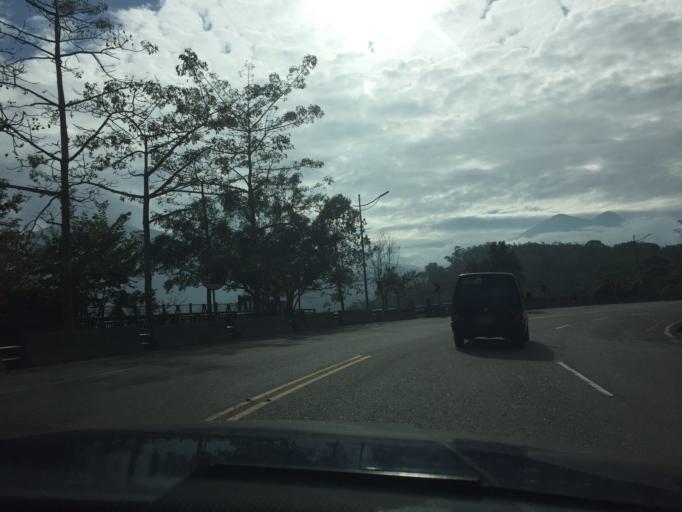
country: TW
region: Taiwan
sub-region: Nantou
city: Puli
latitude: 23.8569
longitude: 120.9019
